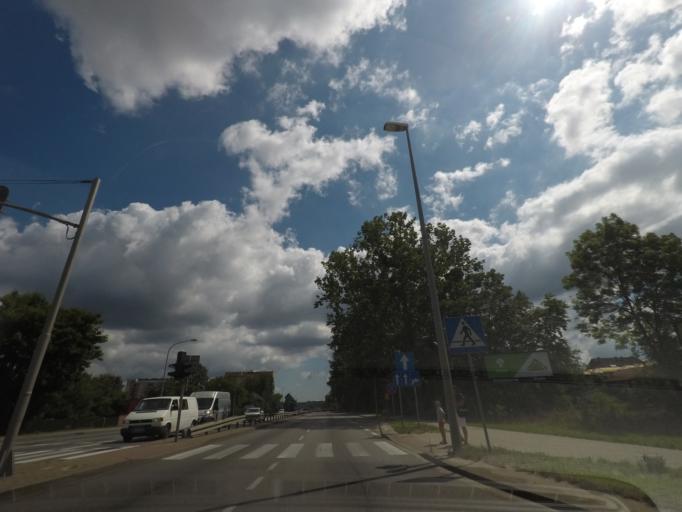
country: PL
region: Pomeranian Voivodeship
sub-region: Powiat wejherowski
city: Wejherowo
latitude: 54.6048
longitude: 18.2423
